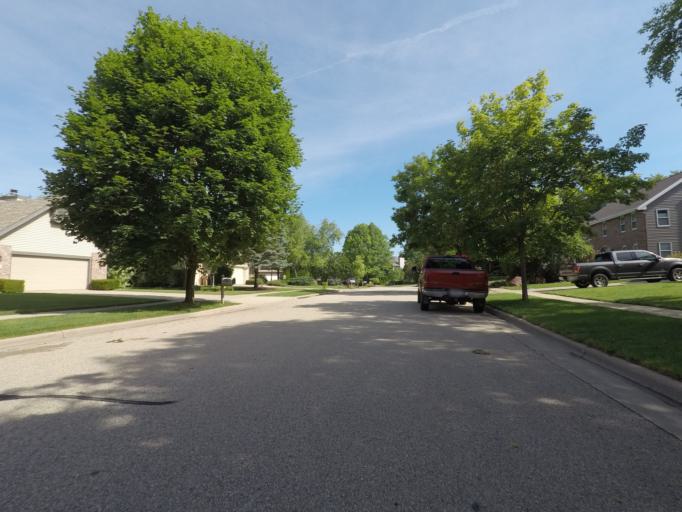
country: US
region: Wisconsin
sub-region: Dane County
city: Middleton
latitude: 43.0786
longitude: -89.4930
